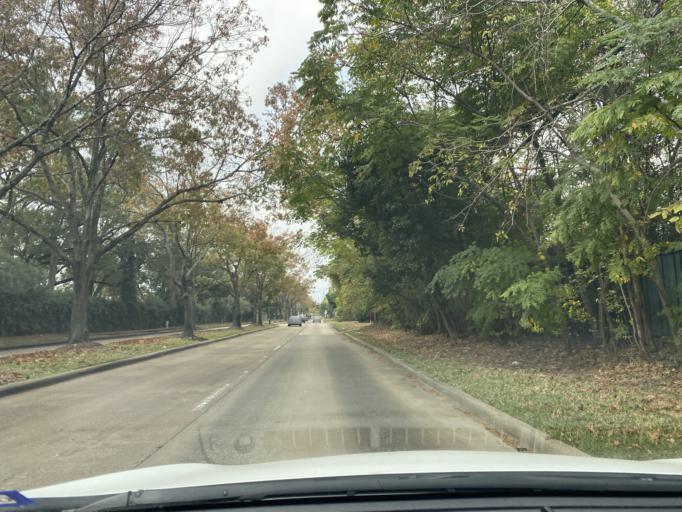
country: US
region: Texas
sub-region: Harris County
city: Hunters Creek Village
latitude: 29.7639
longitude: -95.4727
